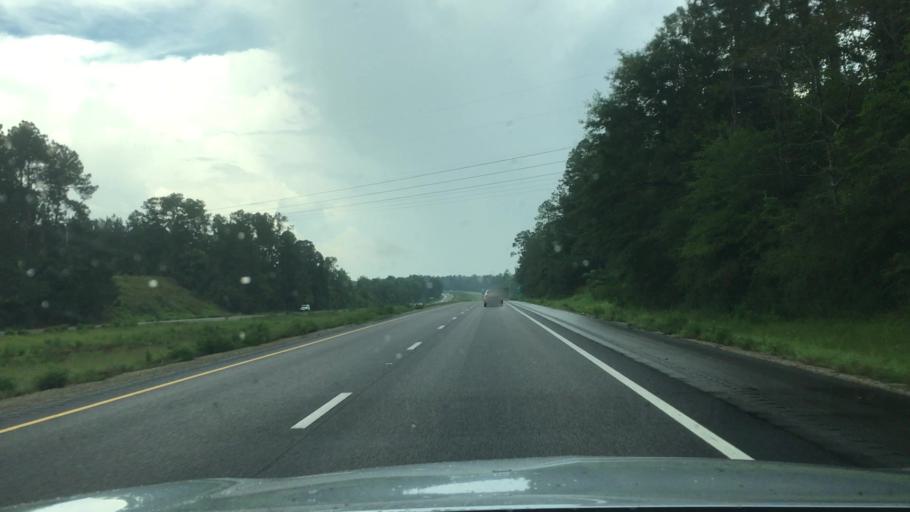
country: US
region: Mississippi
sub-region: Lamar County
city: Purvis
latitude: 31.2161
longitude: -89.3291
